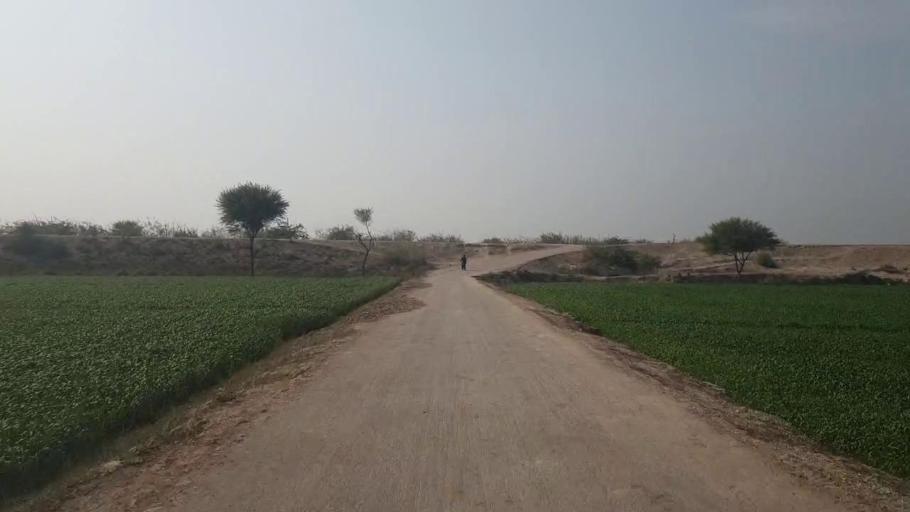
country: PK
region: Sindh
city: Hala
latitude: 25.8115
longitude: 68.4024
